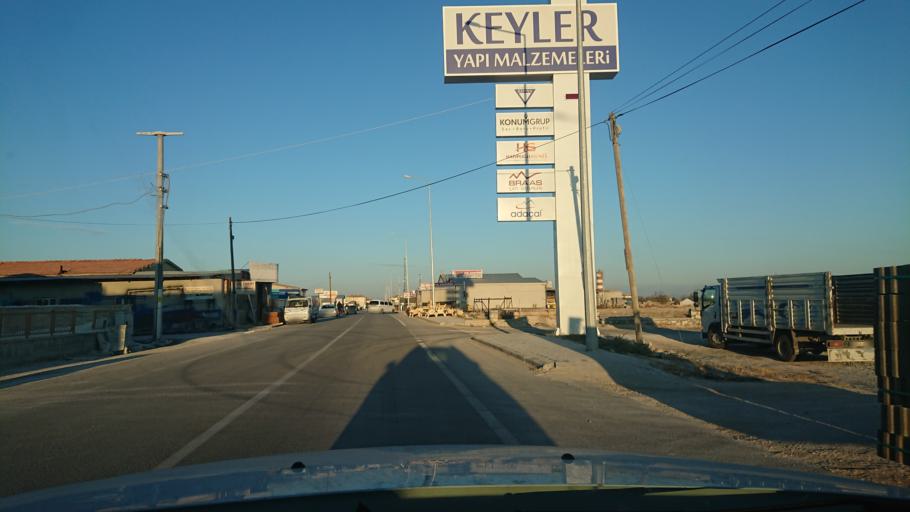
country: TR
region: Aksaray
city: Eskil
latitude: 38.3946
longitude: 33.3963
